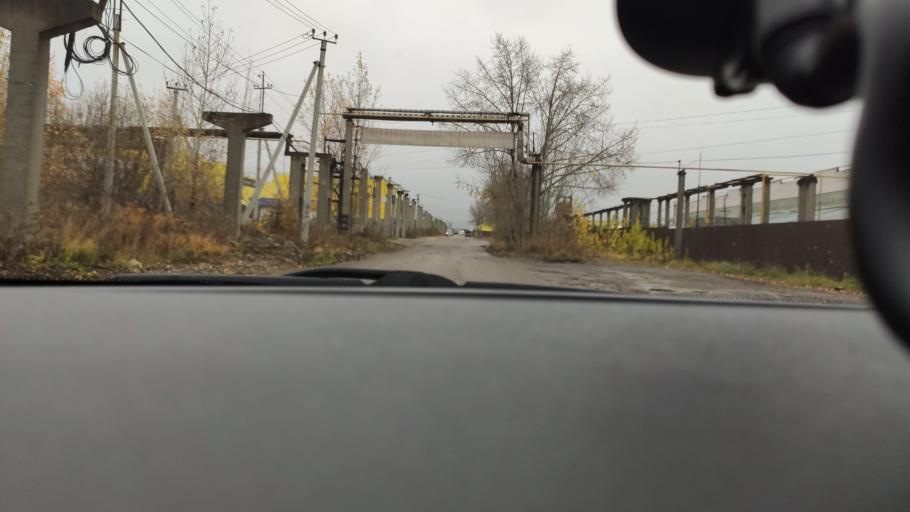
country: RU
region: Perm
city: Gamovo
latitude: 57.9141
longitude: 56.1761
